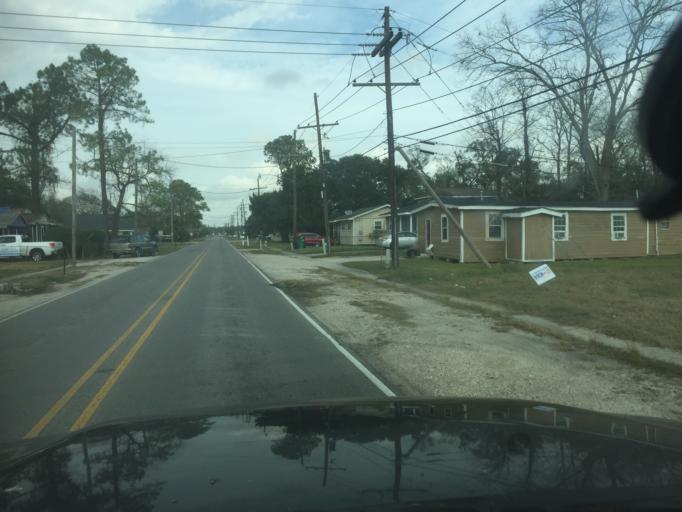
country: US
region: Louisiana
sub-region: Jefferson Parish
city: Waggaman
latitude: 29.9123
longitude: -90.2106
